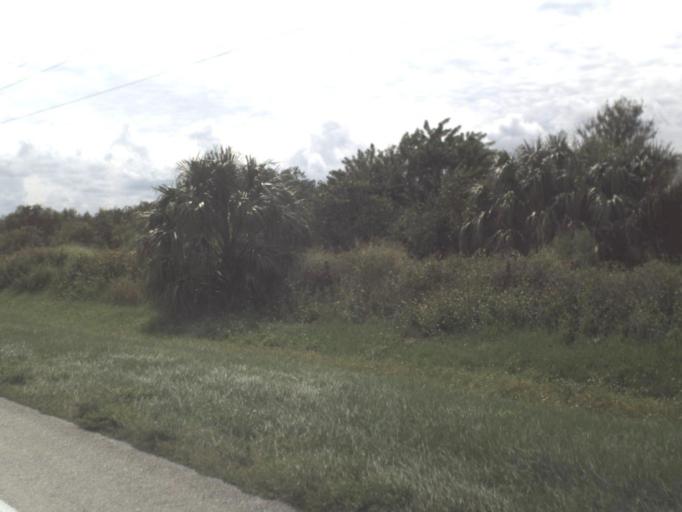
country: US
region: Florida
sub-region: DeSoto County
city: Nocatee
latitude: 27.0889
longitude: -81.7951
